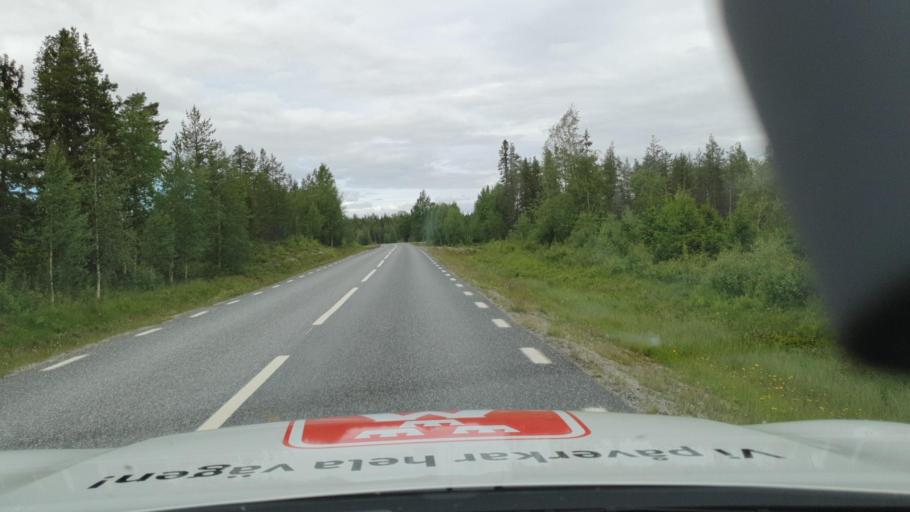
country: SE
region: Vaesterbotten
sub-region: Asele Kommun
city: Insjon
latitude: 64.2509
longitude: 17.5499
